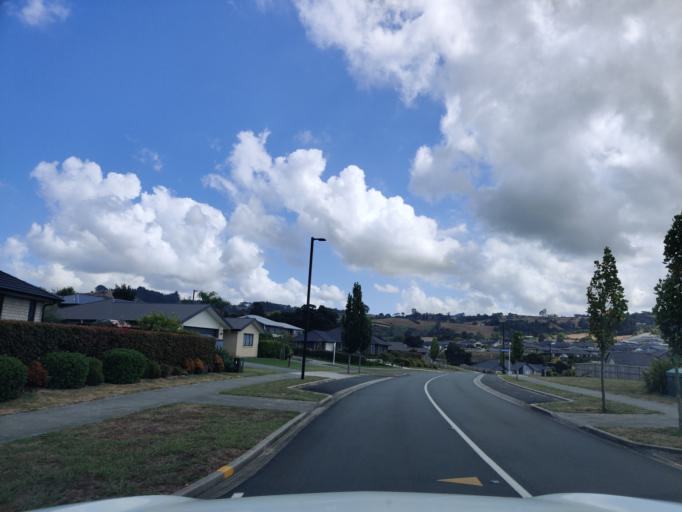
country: NZ
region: Auckland
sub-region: Auckland
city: Pukekohe East
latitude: -37.2360
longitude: 175.0104
